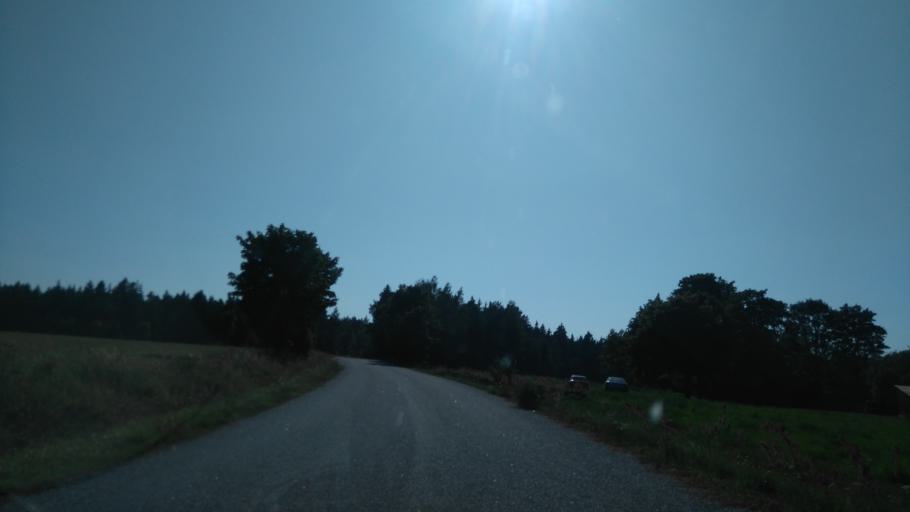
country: EE
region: Saare
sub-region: Kuressaare linn
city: Kuressaare
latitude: 58.5754
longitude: 22.4339
